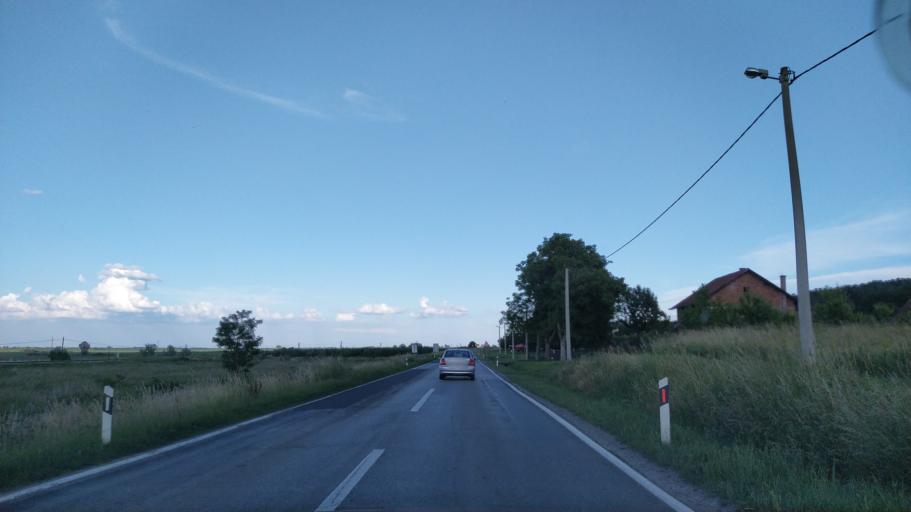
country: HR
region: Virovitick-Podravska
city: Suhopolje
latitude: 45.7482
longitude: 17.5928
